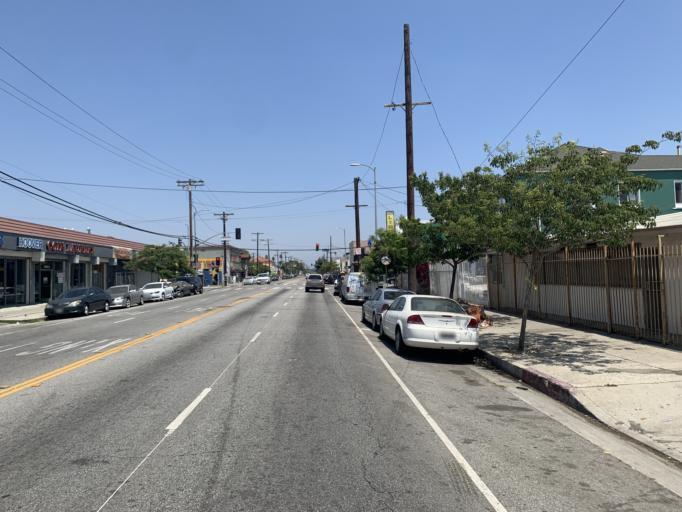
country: US
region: California
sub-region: Los Angeles County
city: Florence-Graham
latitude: 33.9926
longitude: -118.2870
